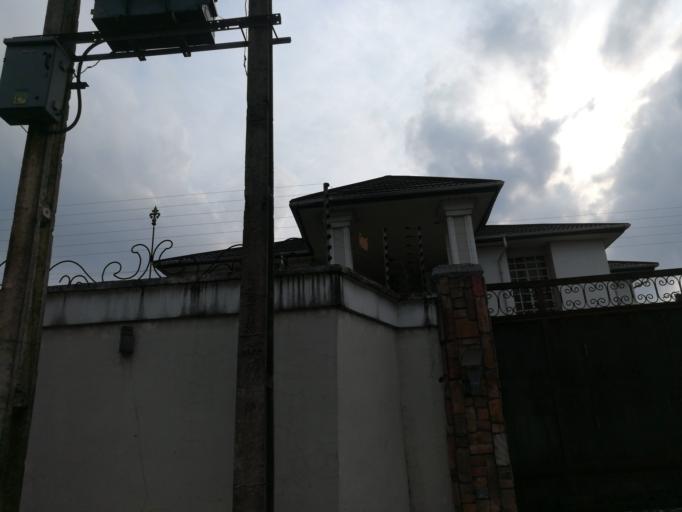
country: NG
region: Rivers
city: Port Harcourt
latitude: 4.8442
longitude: 7.0551
